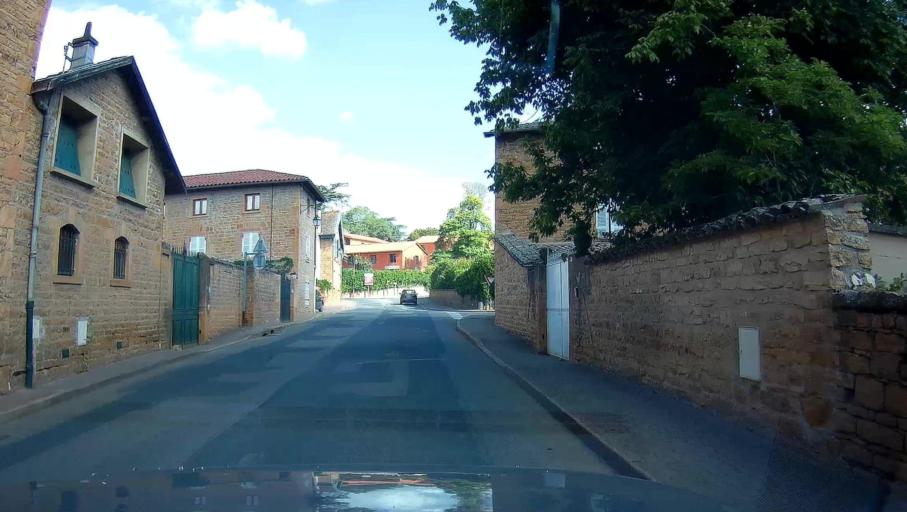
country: FR
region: Rhone-Alpes
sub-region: Departement du Rhone
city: Liergues
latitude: 45.9683
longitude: 4.6679
